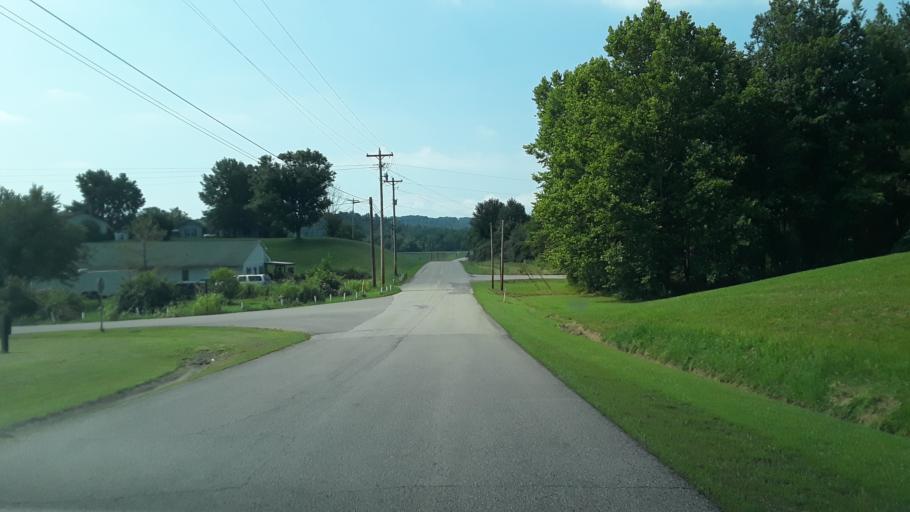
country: US
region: Indiana
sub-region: Clark County
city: Sellersburg
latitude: 38.4577
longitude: -85.8654
